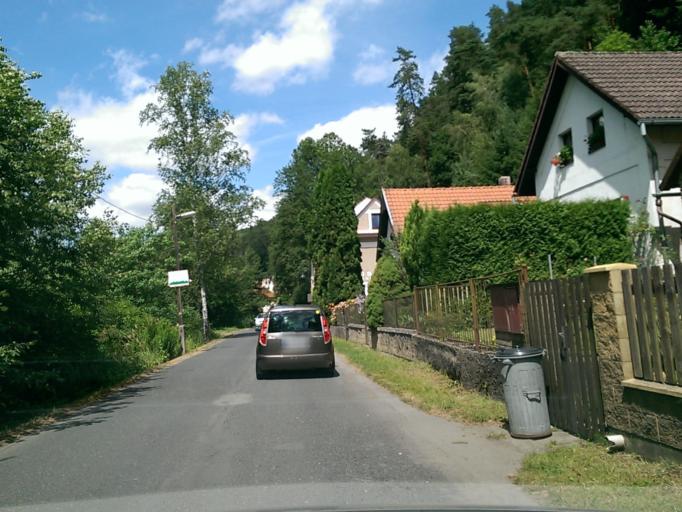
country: CZ
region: Central Bohemia
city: Mseno
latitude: 50.4379
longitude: 14.5807
